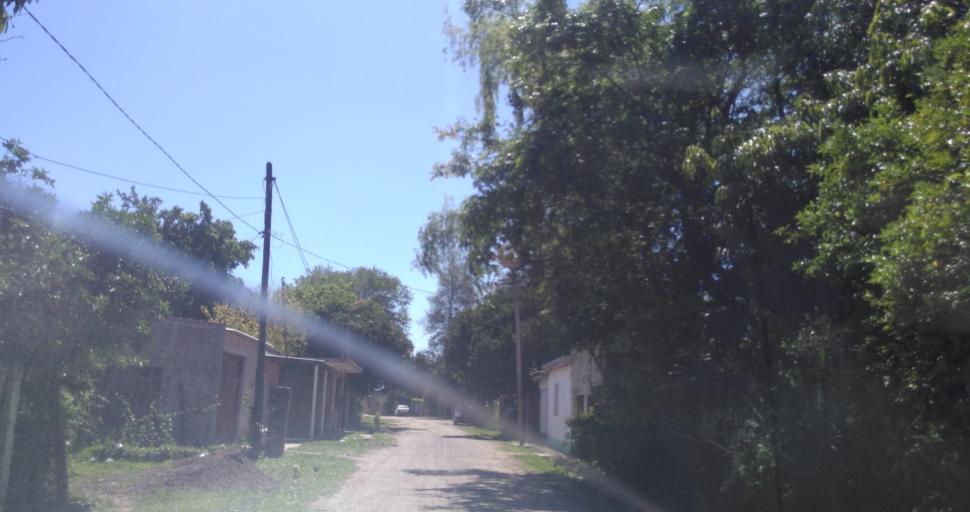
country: AR
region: Chaco
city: Resistencia
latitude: -27.4231
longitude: -58.9807
